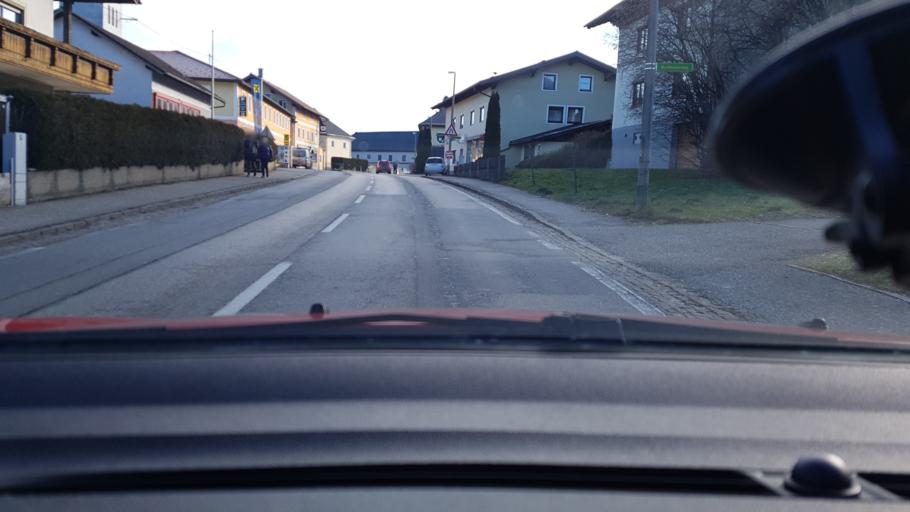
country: AT
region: Salzburg
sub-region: Politischer Bezirk Salzburg-Umgebung
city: Dorfbeuern
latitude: 48.0464
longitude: 12.9885
